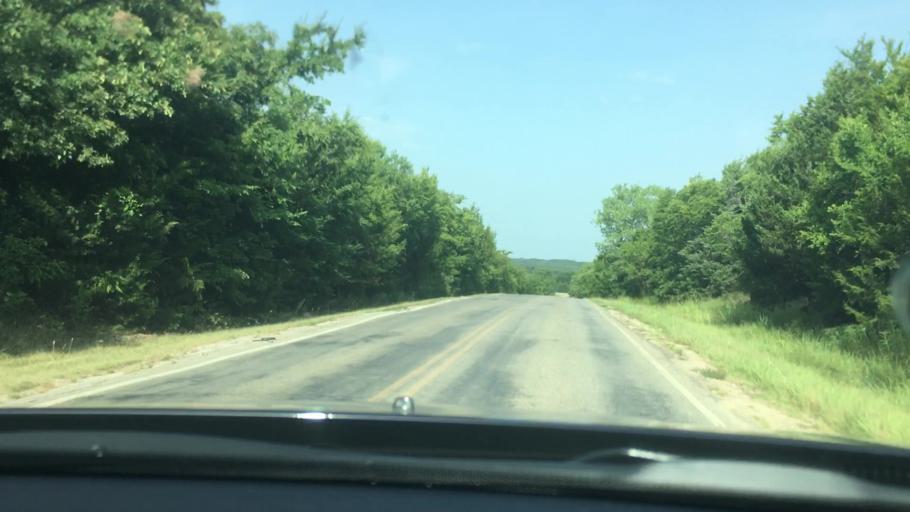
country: US
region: Oklahoma
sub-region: Pontotoc County
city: Byng
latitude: 34.8648
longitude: -96.6159
